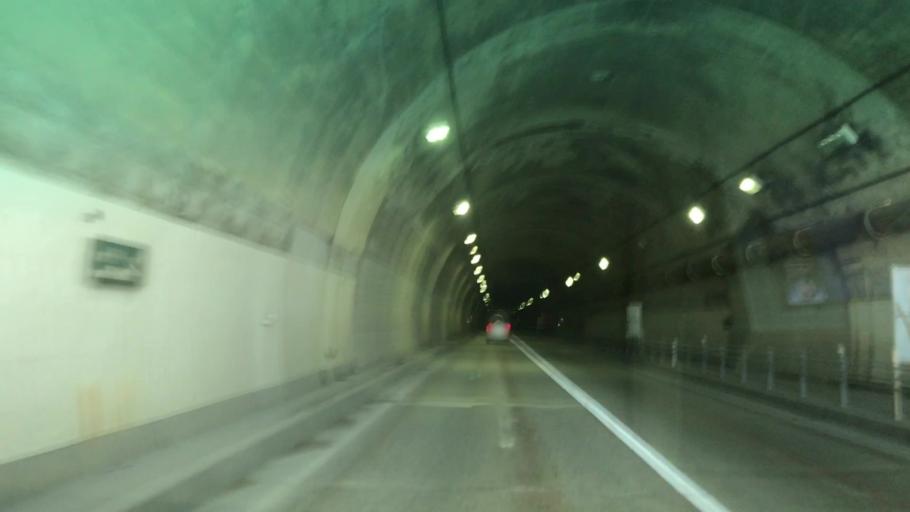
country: JP
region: Hokkaido
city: Iwanai
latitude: 43.0411
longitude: 140.5125
